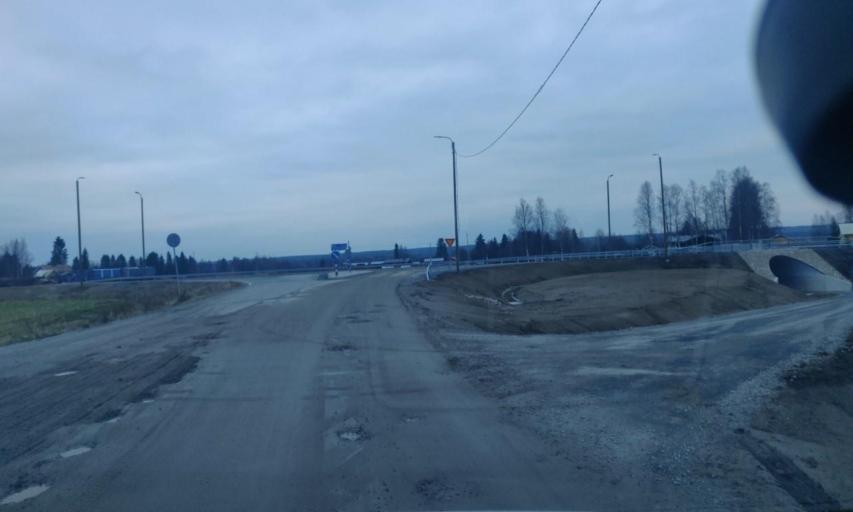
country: FI
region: Northern Ostrobothnia
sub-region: Oulu
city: Muhos
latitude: 64.7920
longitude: 26.0762
